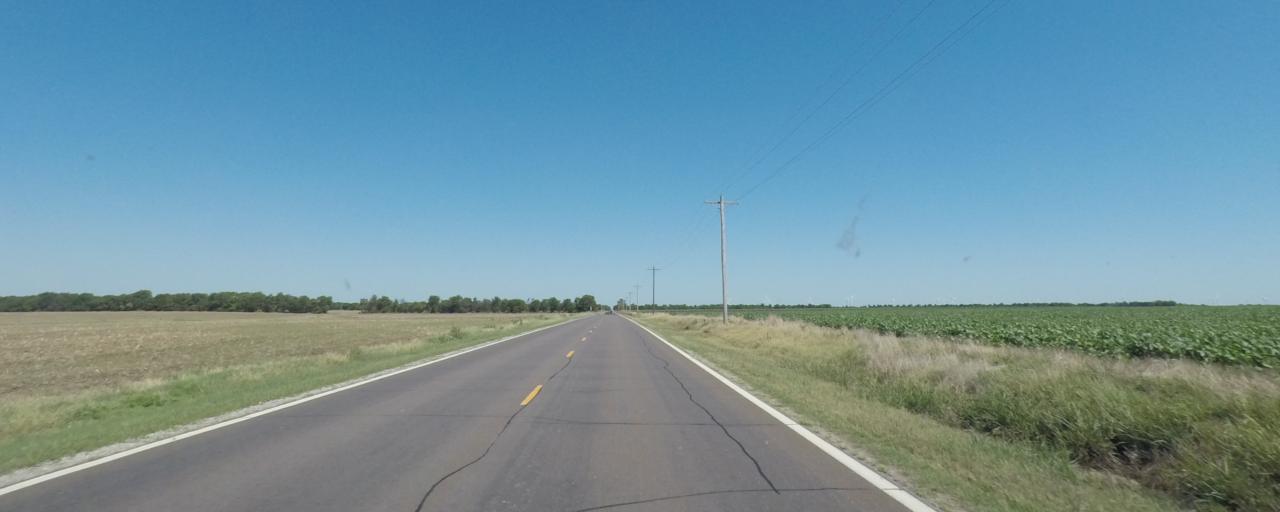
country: US
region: Kansas
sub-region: Sumner County
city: Wellington
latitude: 37.0925
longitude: -97.4015
